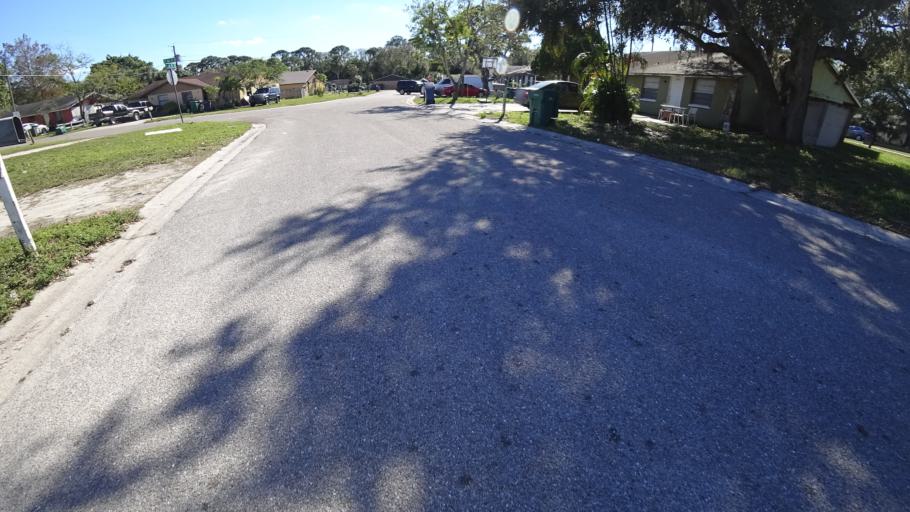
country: US
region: Florida
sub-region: Manatee County
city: Whitfield
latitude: 27.4383
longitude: -82.5545
